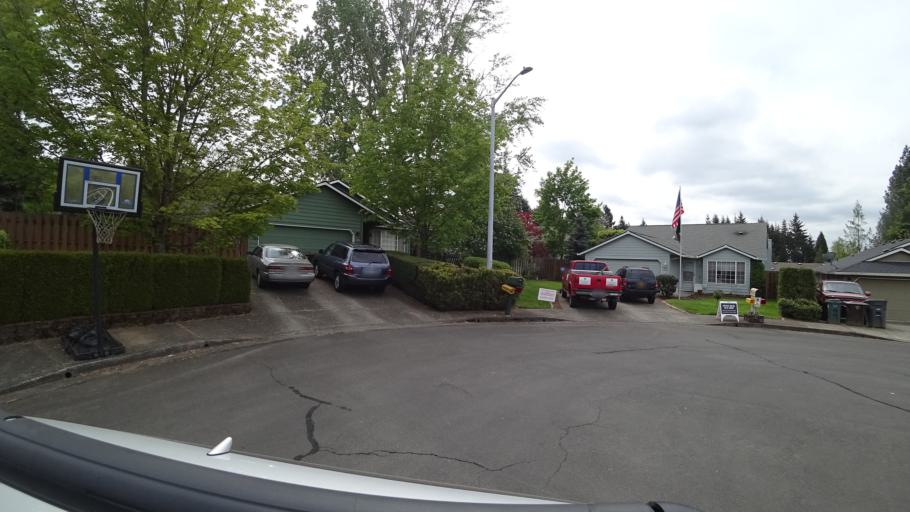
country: US
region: Oregon
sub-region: Washington County
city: Hillsboro
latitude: 45.5269
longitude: -123.0008
